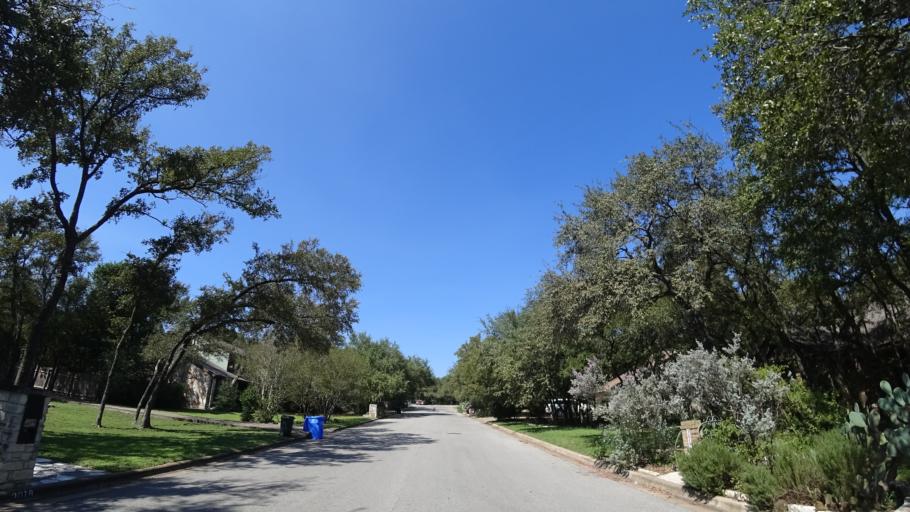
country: US
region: Texas
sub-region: Travis County
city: Rollingwood
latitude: 30.2795
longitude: -97.7871
